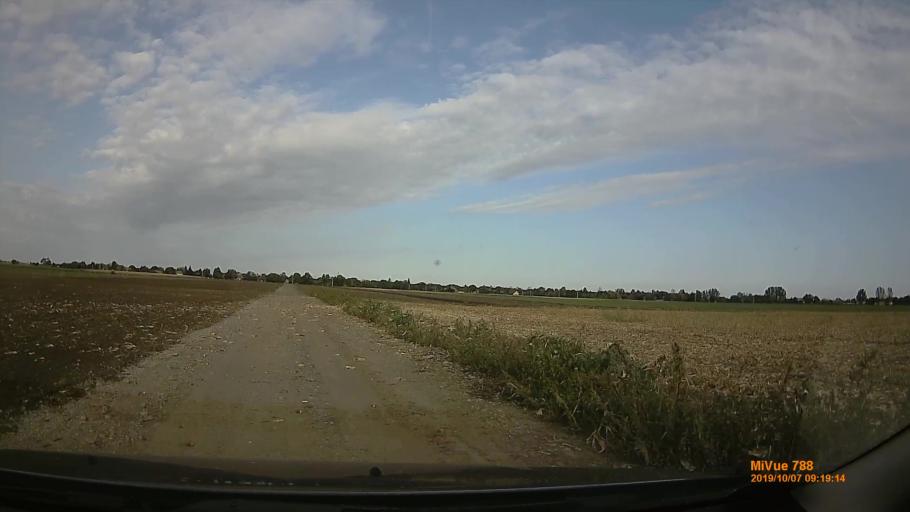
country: HU
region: Bekes
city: Szarvas
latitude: 46.8149
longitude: 20.6640
